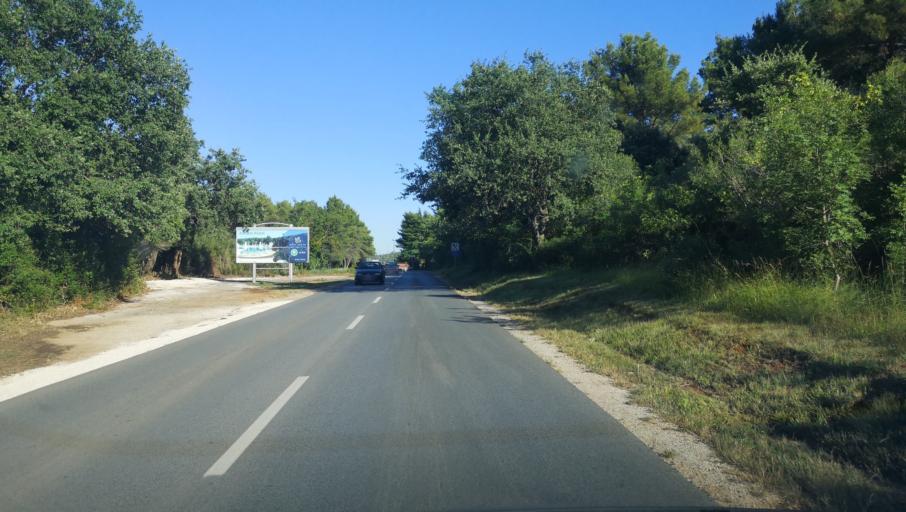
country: HR
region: Istarska
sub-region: Grad Rovinj
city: Rovinj
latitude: 45.0666
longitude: 13.6870
